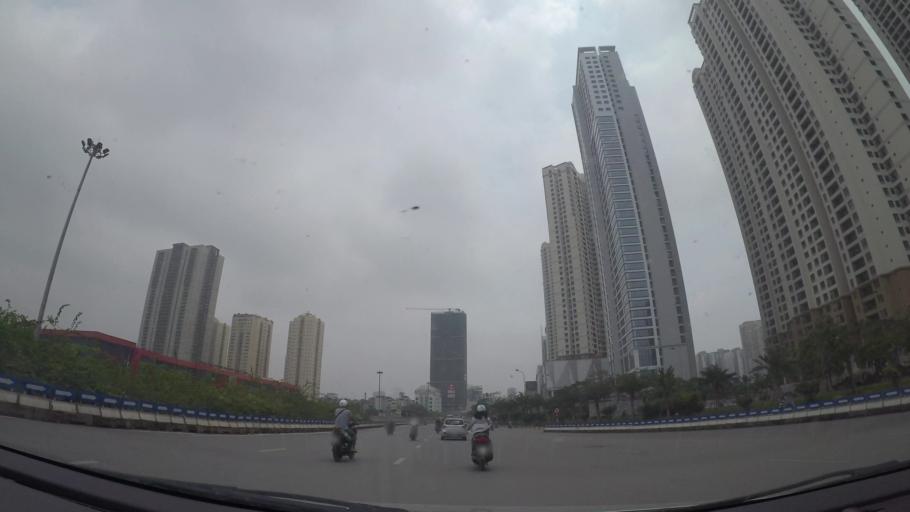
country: VN
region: Ha Noi
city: Thanh Xuan
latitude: 21.0052
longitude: 105.7931
